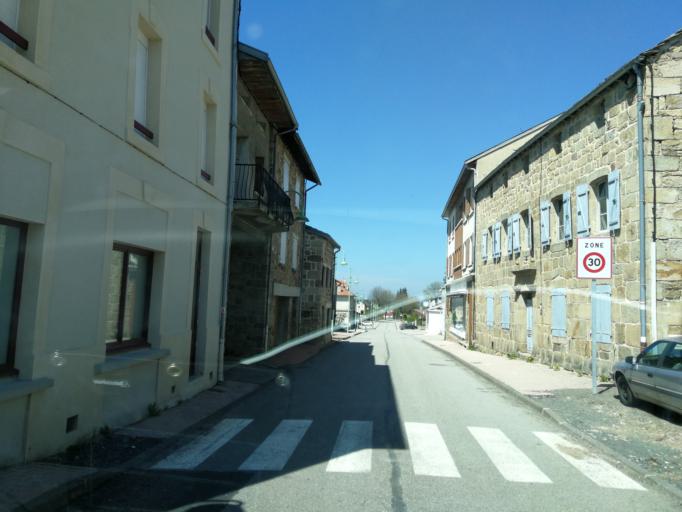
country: FR
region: Rhone-Alpes
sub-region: Departement de l'Ardeche
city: Saint-Agreve
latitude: 45.0103
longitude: 4.3948
